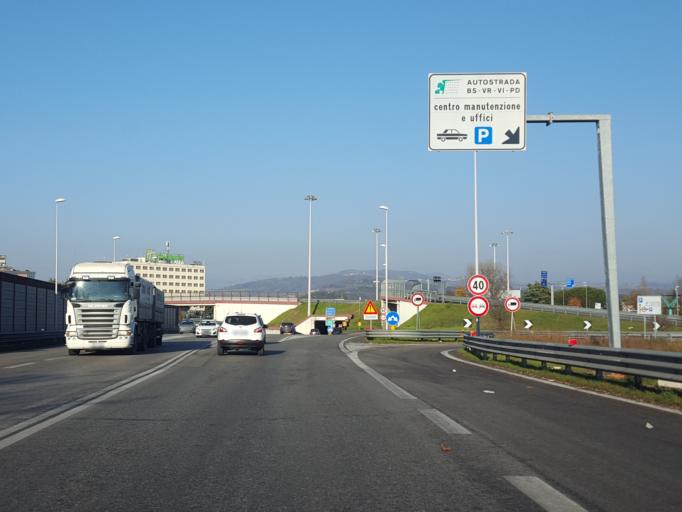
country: IT
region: Veneto
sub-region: Provincia di Verona
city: San Martino Buon Albergo
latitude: 45.4121
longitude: 11.0871
